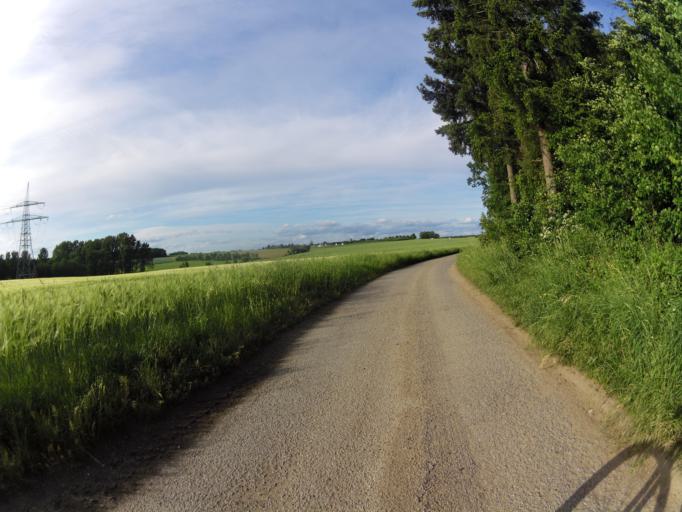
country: DE
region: Bavaria
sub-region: Regierungsbezirk Unterfranken
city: Frickenhausen
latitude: 49.6982
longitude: 10.0726
